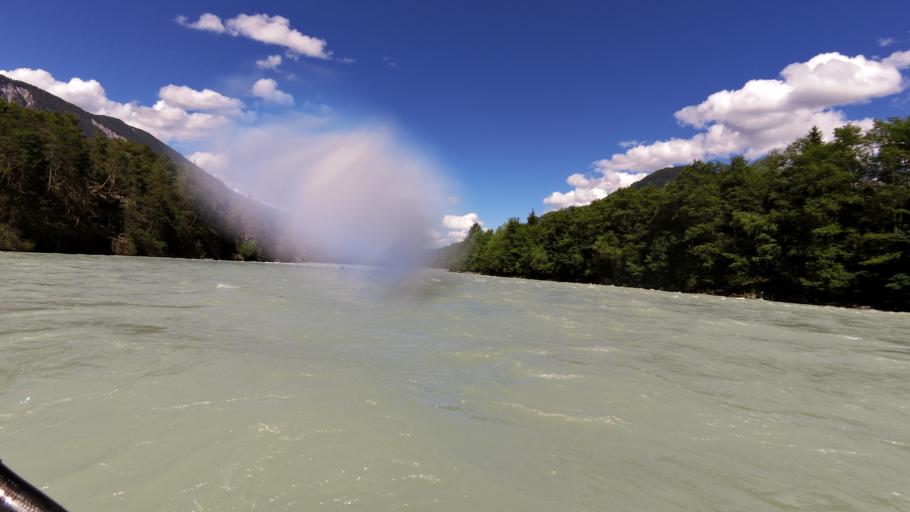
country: AT
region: Tyrol
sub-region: Politischer Bezirk Imst
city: Roppen
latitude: 47.2259
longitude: 10.8278
